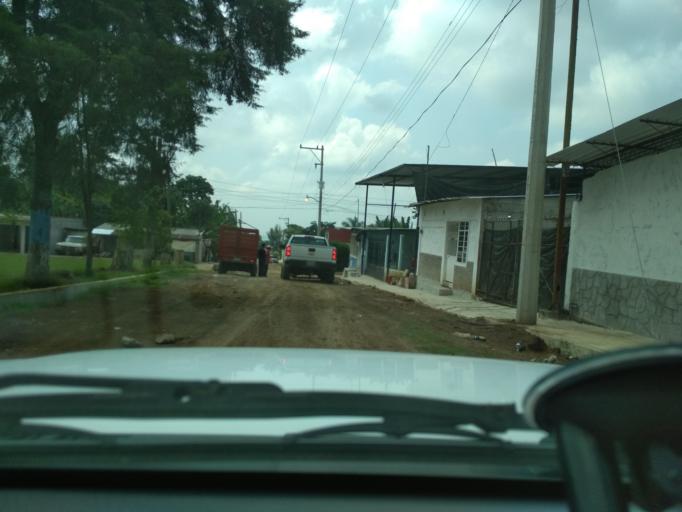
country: MX
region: Veracruz
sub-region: Fortin
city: Santa Lucia Potrerillo
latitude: 18.9687
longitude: -97.0258
